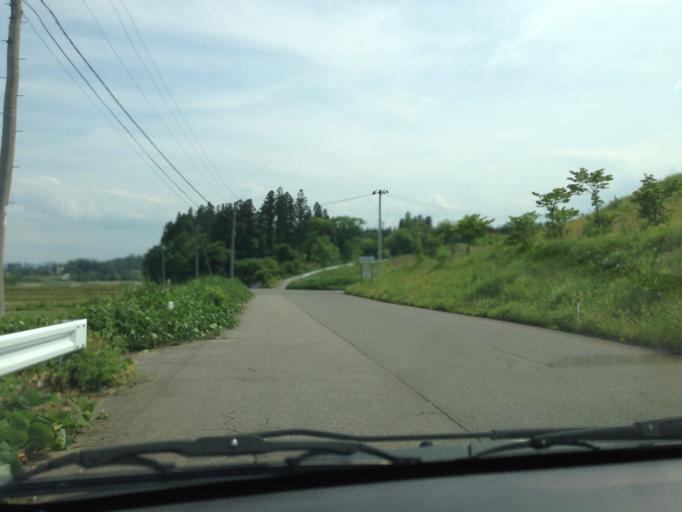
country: JP
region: Fukushima
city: Kitakata
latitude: 37.5178
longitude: 139.8077
